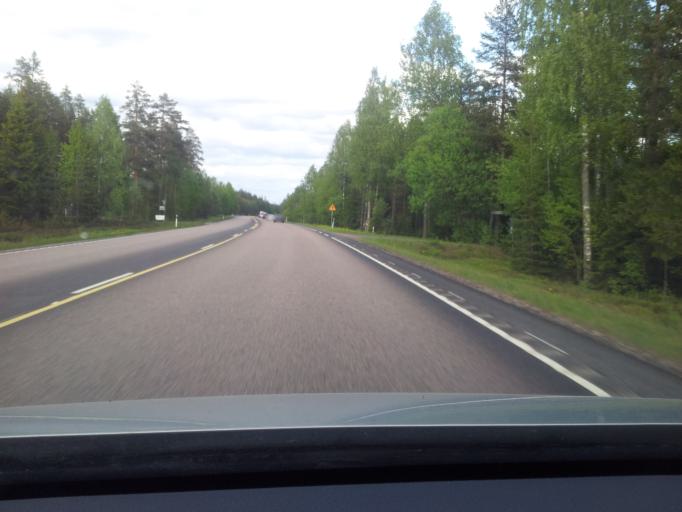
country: FI
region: South Karelia
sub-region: Lappeenranta
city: Taavetti
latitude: 60.9138
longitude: 27.3971
